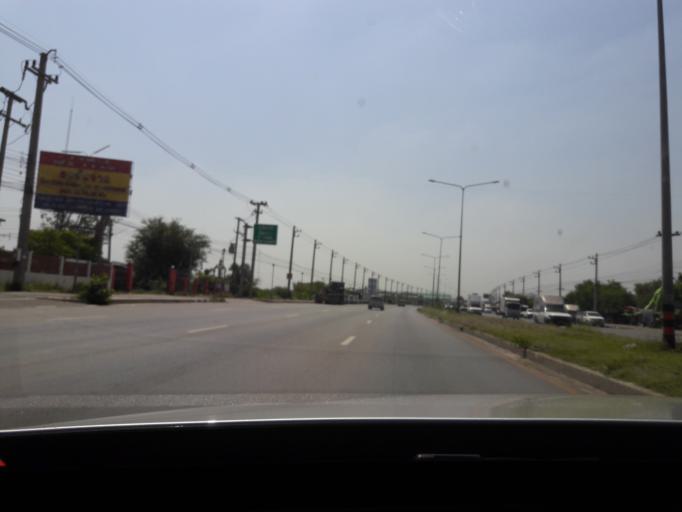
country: TH
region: Samut Sakhon
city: Krathum Baen
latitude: 13.6616
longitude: 100.3129
